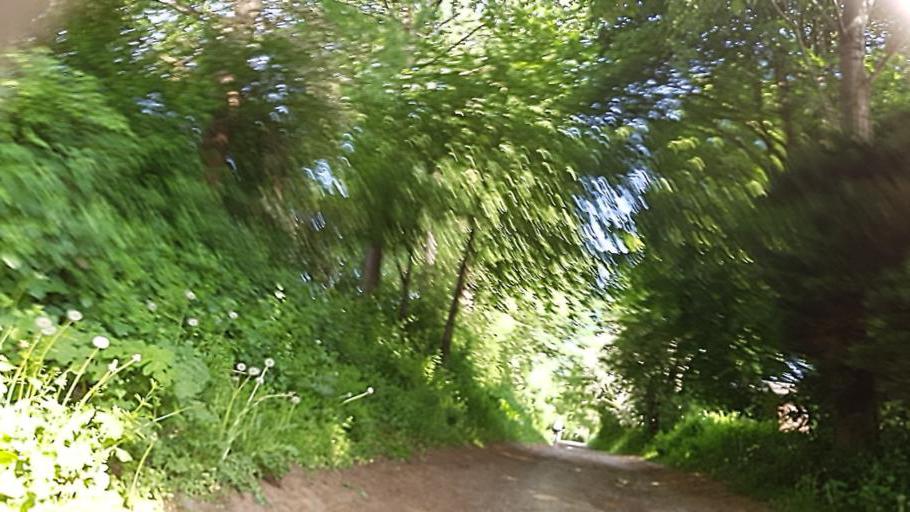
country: BE
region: Flanders
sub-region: Provincie Vlaams-Brabant
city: Huldenberg
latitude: 50.7937
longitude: 4.5779
